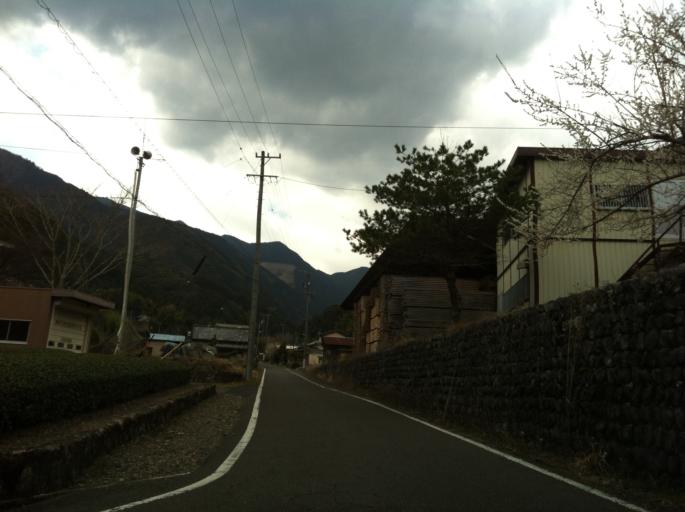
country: JP
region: Shizuoka
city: Shizuoka-shi
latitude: 35.0692
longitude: 138.3140
